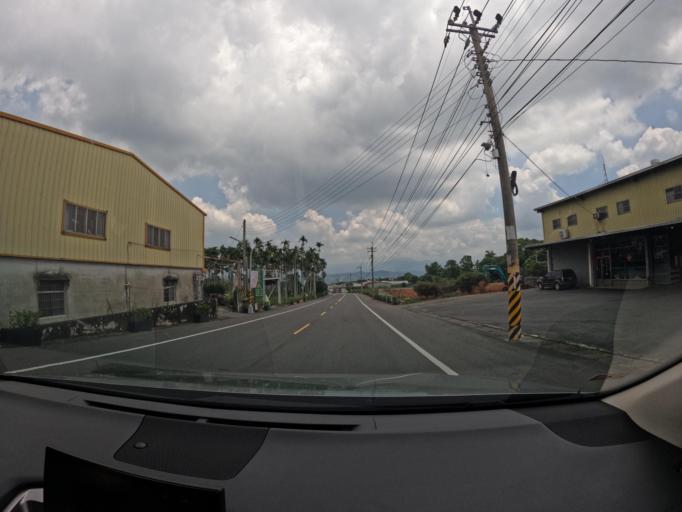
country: TW
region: Taiwan
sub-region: Nantou
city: Nantou
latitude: 23.8309
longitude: 120.6516
